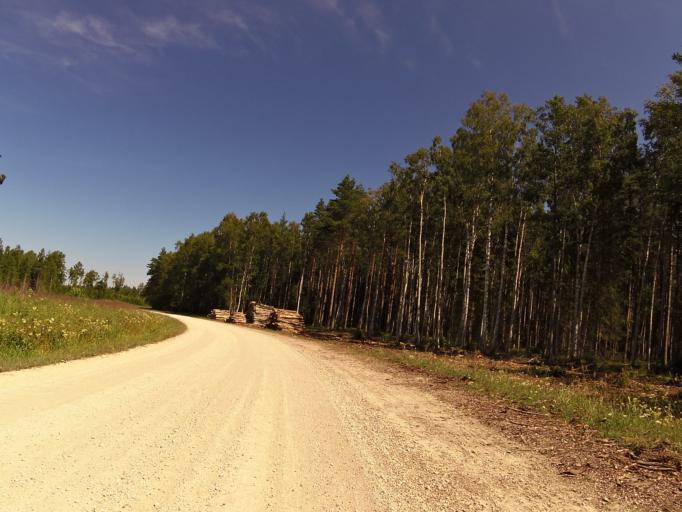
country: EE
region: Hiiumaa
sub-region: Kaerdla linn
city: Kardla
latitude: 58.9241
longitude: 22.3676
